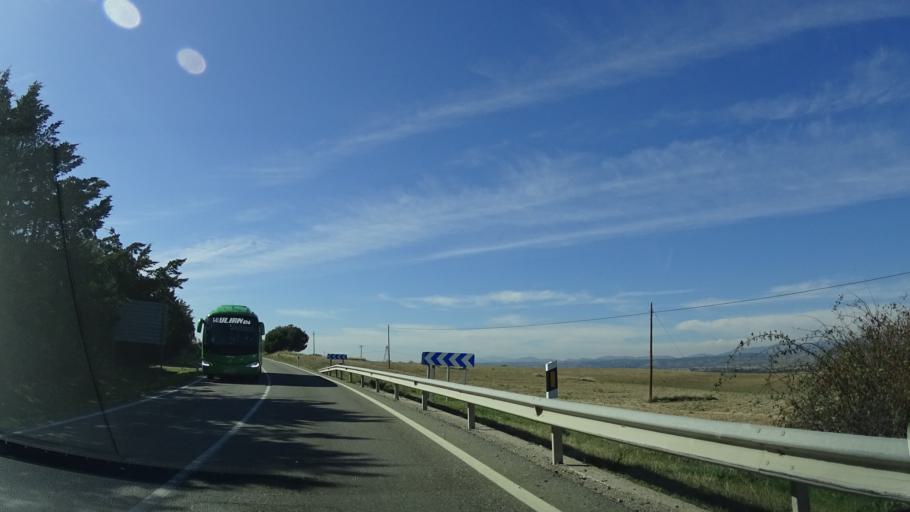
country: ES
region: Madrid
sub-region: Provincia de Madrid
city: Las Rozas de Madrid
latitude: 40.4953
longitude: -3.9088
